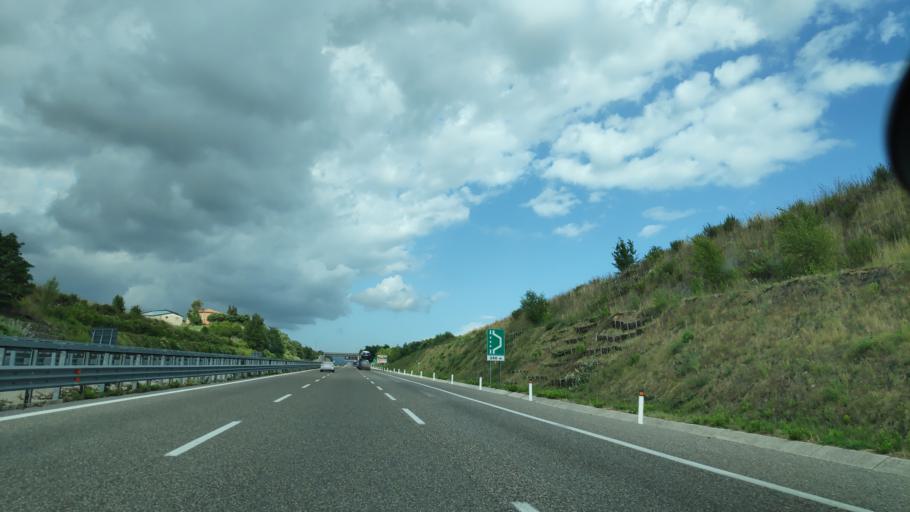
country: IT
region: Campania
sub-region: Provincia di Salerno
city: Contursi Terme
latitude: 40.6133
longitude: 15.2609
